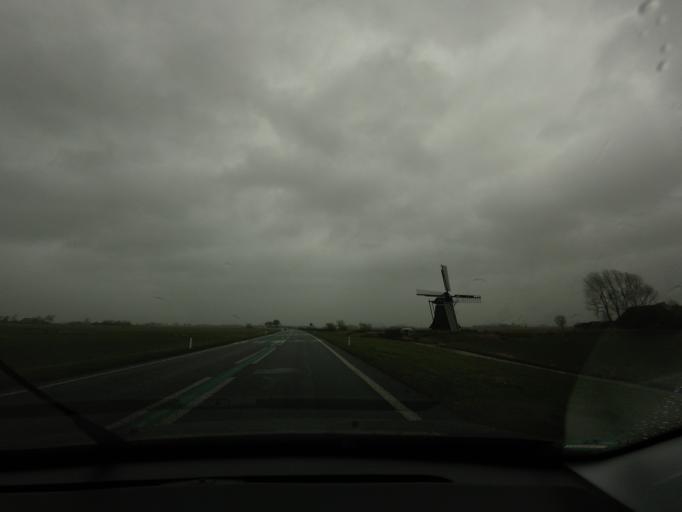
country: NL
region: Friesland
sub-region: Gemeente Littenseradiel
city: Wommels
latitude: 53.0981
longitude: 5.5583
